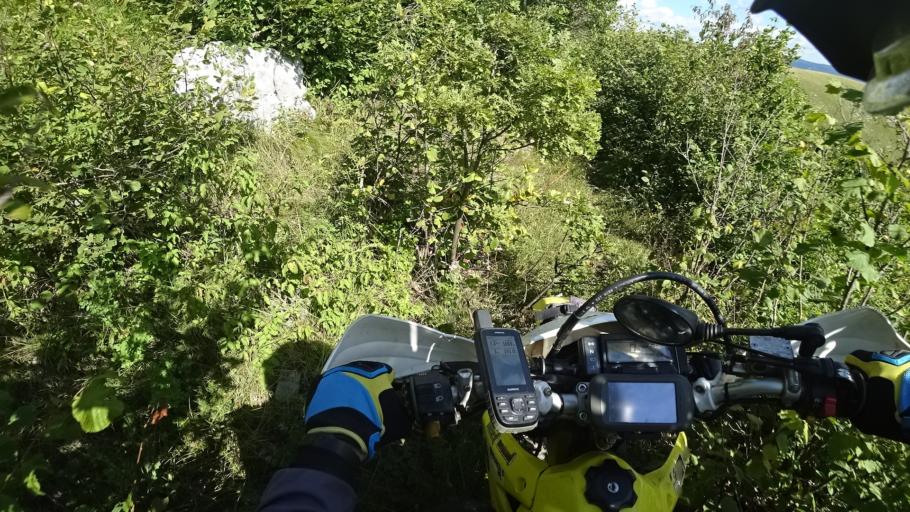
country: HR
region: Zadarska
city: Gracac
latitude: 44.3799
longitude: 16.0491
